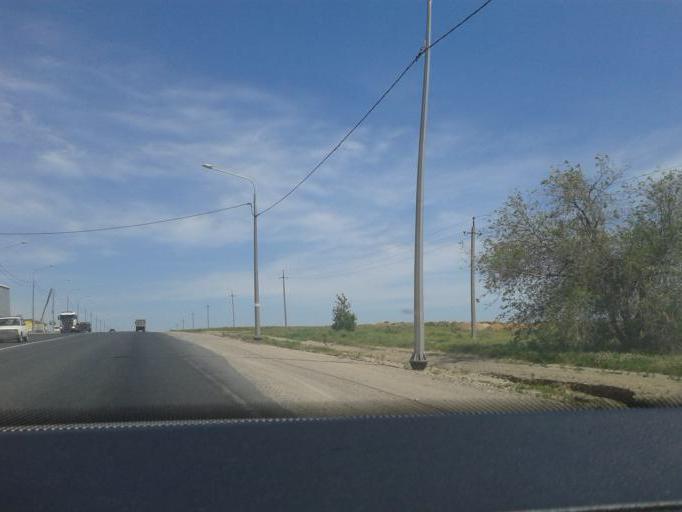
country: RU
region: Volgograd
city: Vodstroy
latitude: 48.8126
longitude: 44.5241
